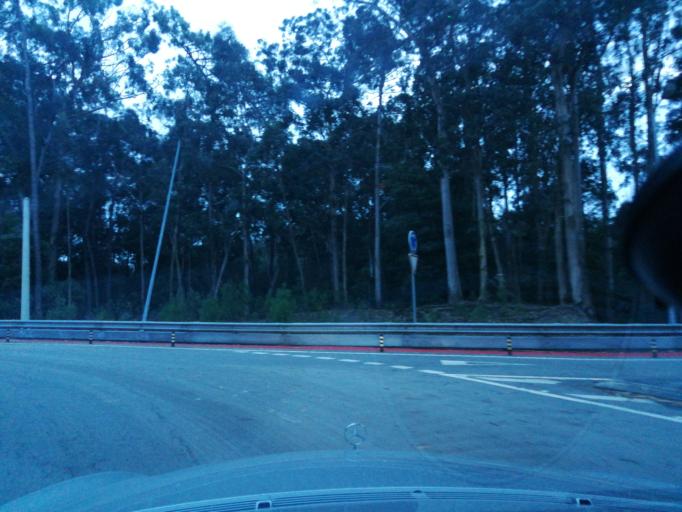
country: PT
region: Aveiro
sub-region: Estarreja
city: Estarreja
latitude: 40.7591
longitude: -8.6035
